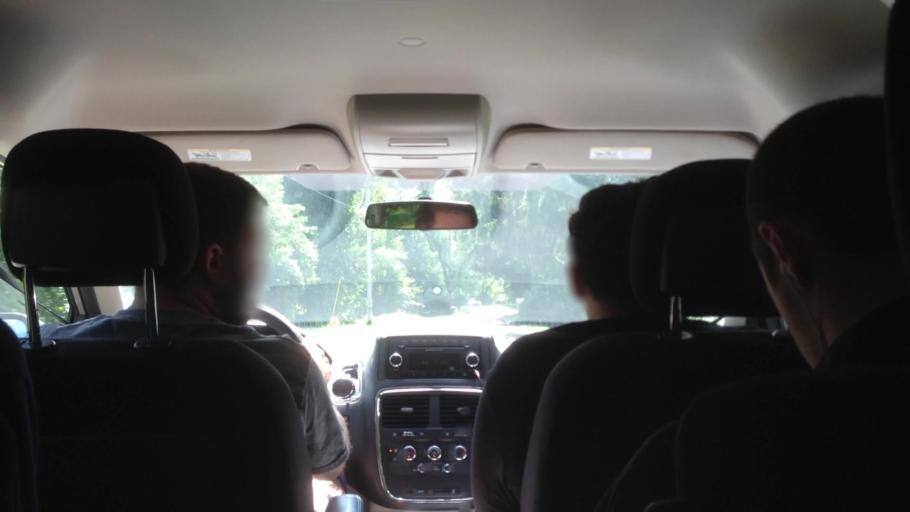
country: US
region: New York
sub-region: Dutchess County
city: Tivoli
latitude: 42.1169
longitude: -73.8930
